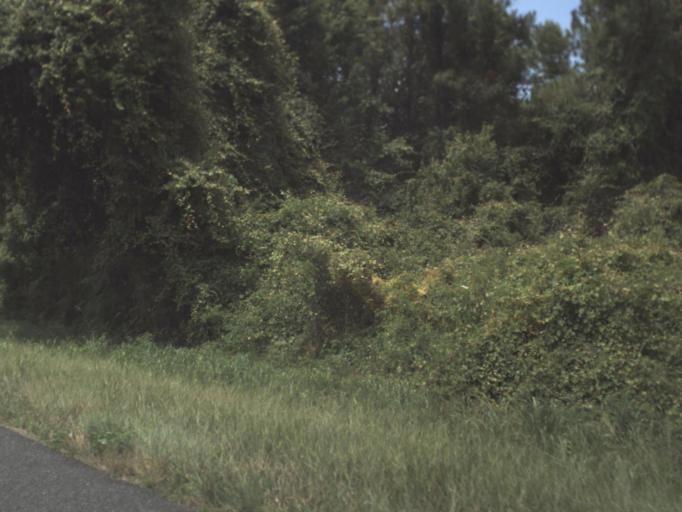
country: US
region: Florida
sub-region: Taylor County
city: Perry
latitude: 30.2382
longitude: -83.6890
